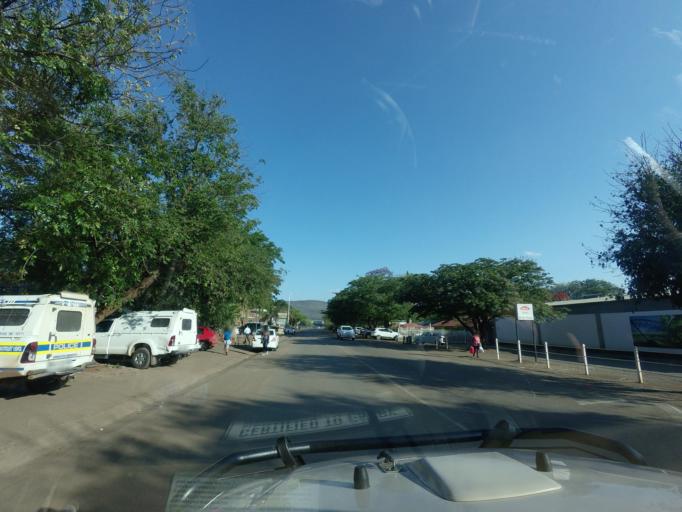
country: ZA
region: Mpumalanga
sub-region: Ehlanzeni District
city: Komatipoort
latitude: -25.4366
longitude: 31.9574
